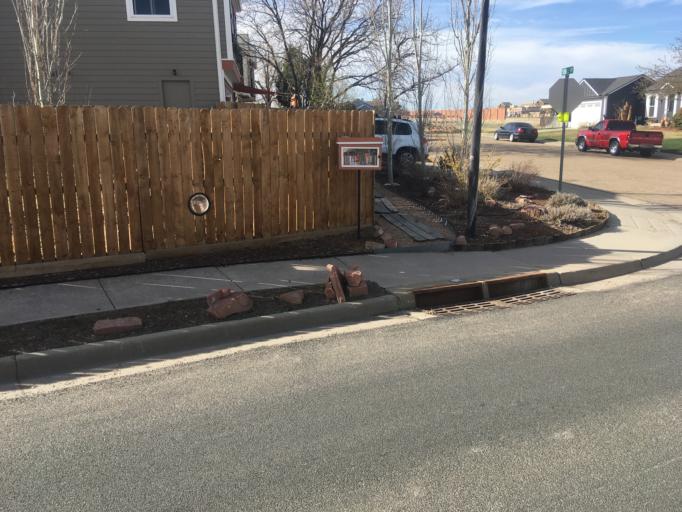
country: US
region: Colorado
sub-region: Boulder County
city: Lafayette
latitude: 40.0104
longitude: -105.1020
